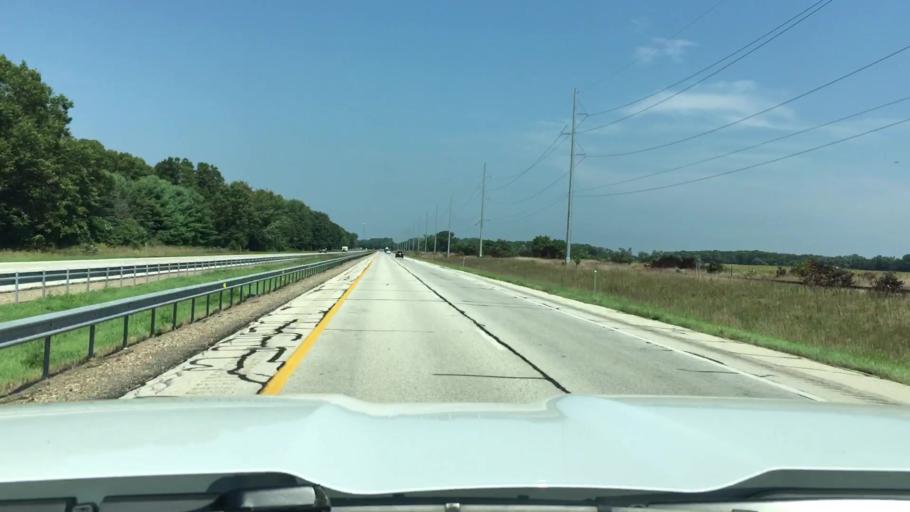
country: US
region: Michigan
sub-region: Saint Joseph County
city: Three Rivers
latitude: 42.0011
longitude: -85.6334
